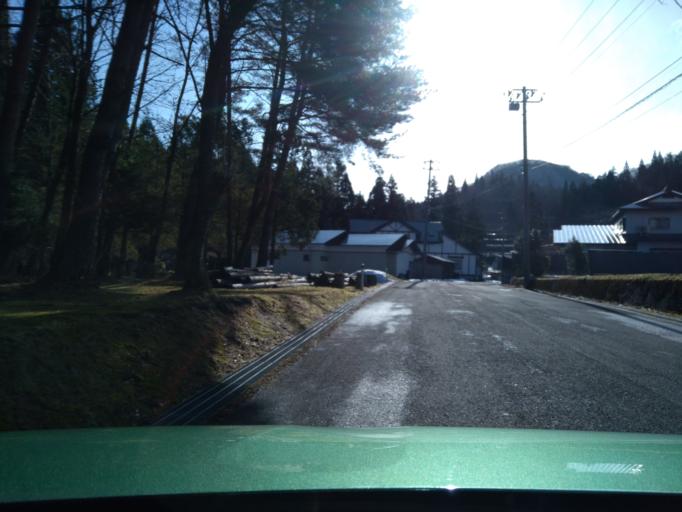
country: JP
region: Iwate
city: Hanamaki
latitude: 39.4505
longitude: 141.0047
